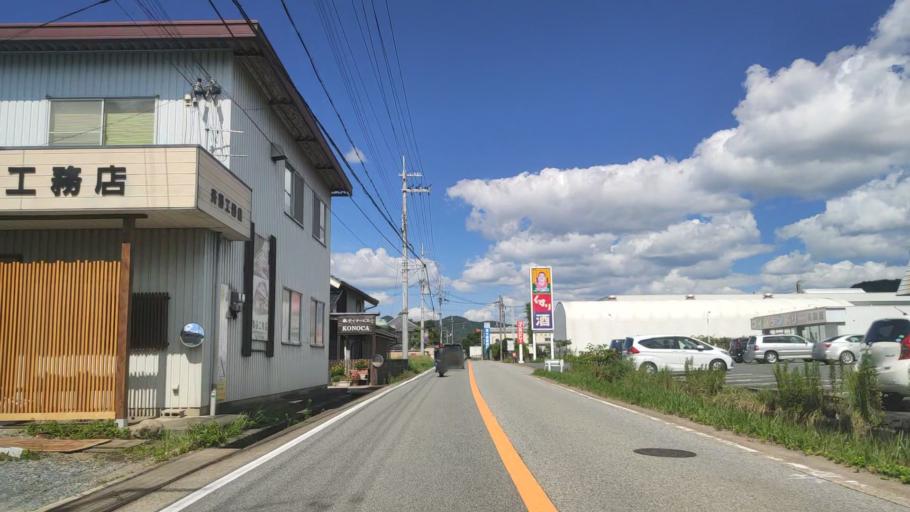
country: JP
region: Kyoto
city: Fukuchiyama
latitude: 35.2224
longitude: 135.1302
